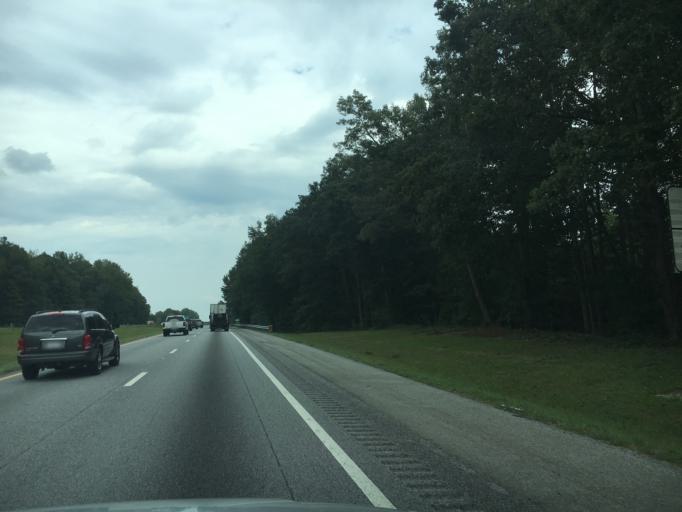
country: US
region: Georgia
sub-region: Hart County
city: Reed Creek
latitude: 34.5141
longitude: -82.8957
